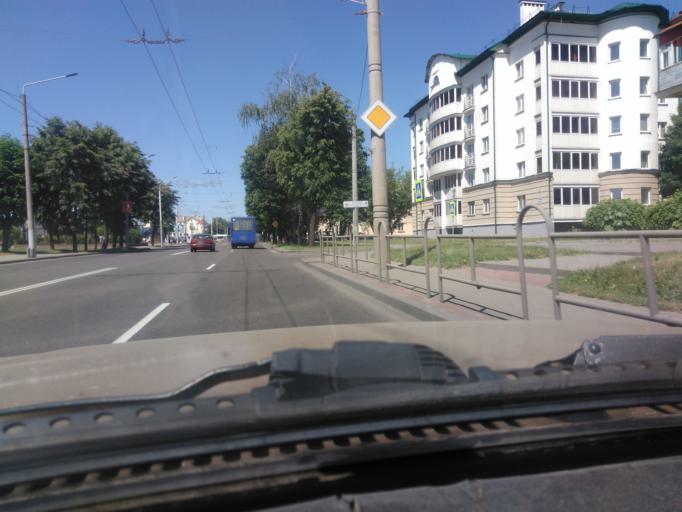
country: BY
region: Mogilev
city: Mahilyow
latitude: 53.9244
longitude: 30.3413
